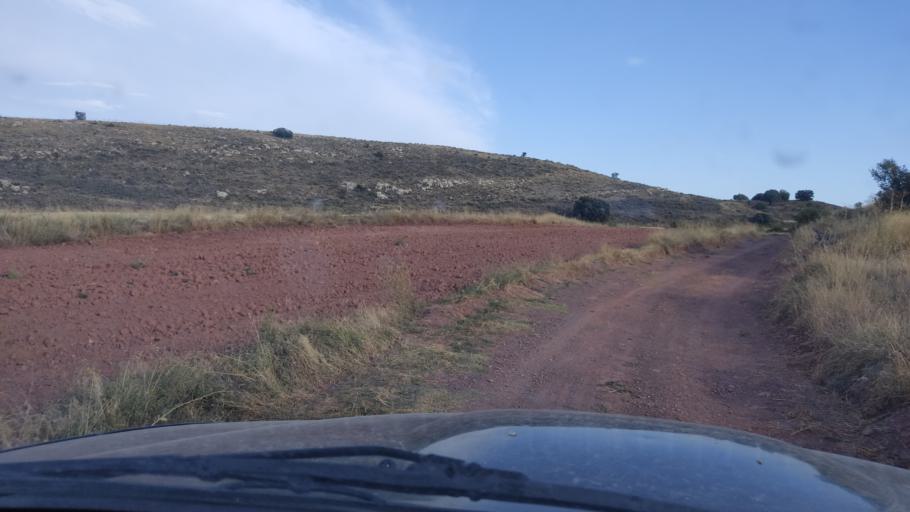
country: ES
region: Aragon
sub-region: Provincia de Teruel
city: Monforte de Moyuela
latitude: 41.0278
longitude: -1.0078
